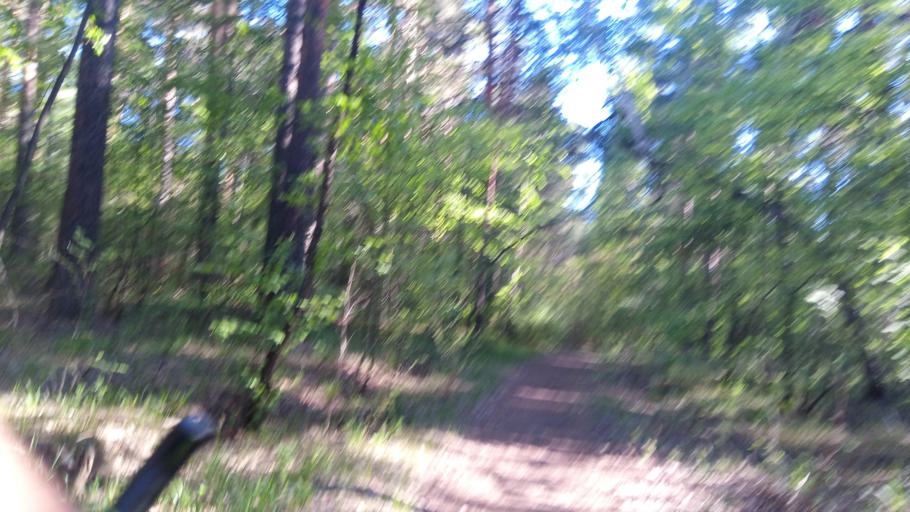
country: RU
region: Chelyabinsk
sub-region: Gorod Chelyabinsk
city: Chelyabinsk
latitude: 55.1499
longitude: 61.3467
